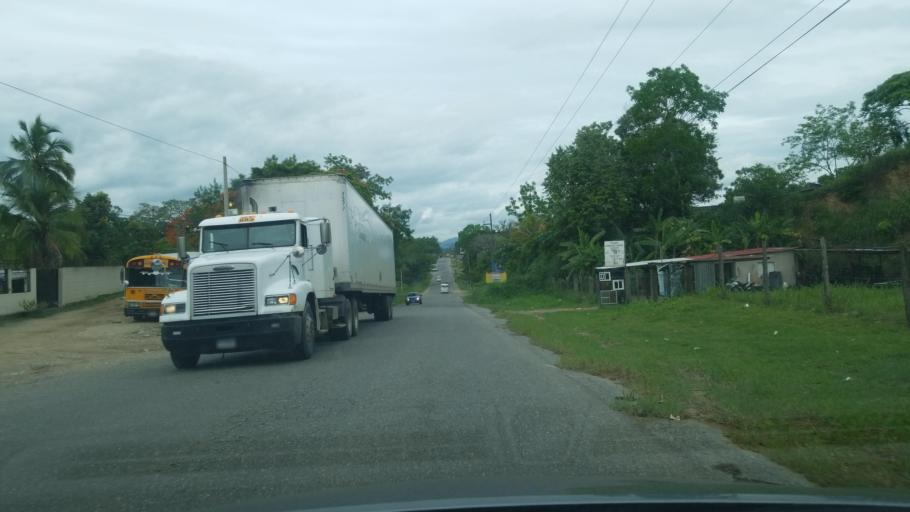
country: HN
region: Santa Barbara
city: La Flecha
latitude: 15.2985
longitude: -88.4829
